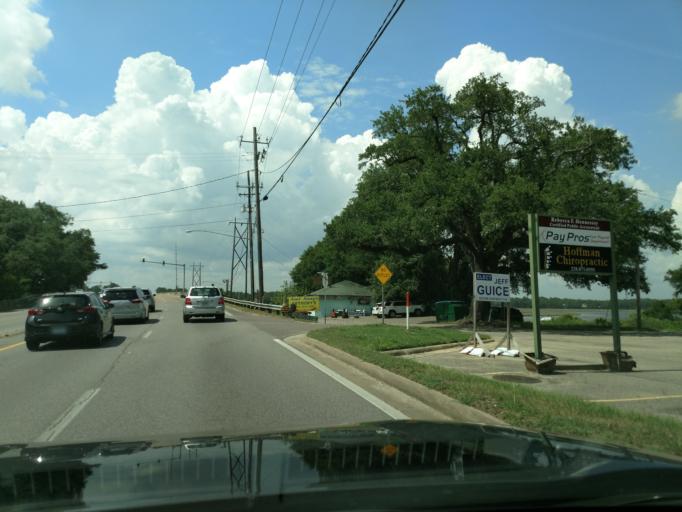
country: US
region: Mississippi
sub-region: Jackson County
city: Ocean Springs
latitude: 30.4179
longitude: -88.8275
